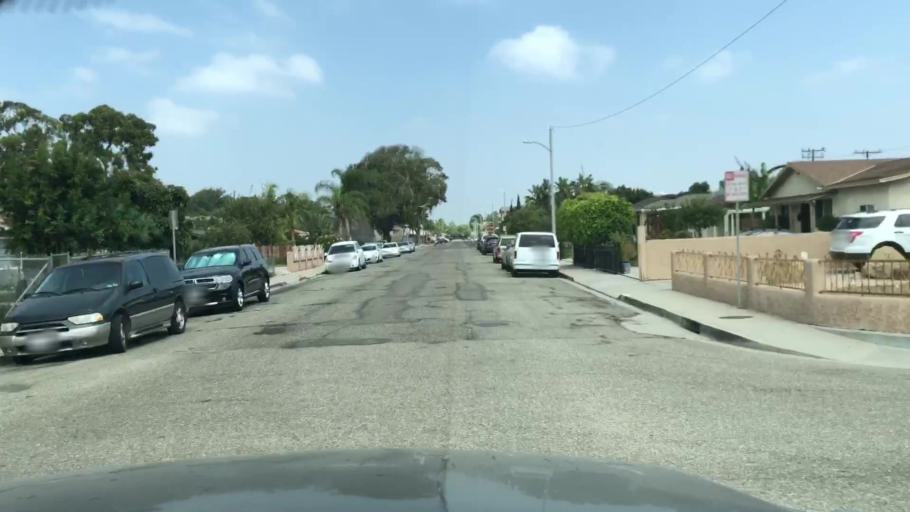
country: US
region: California
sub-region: Ventura County
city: Oxnard
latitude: 34.2016
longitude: -119.1664
